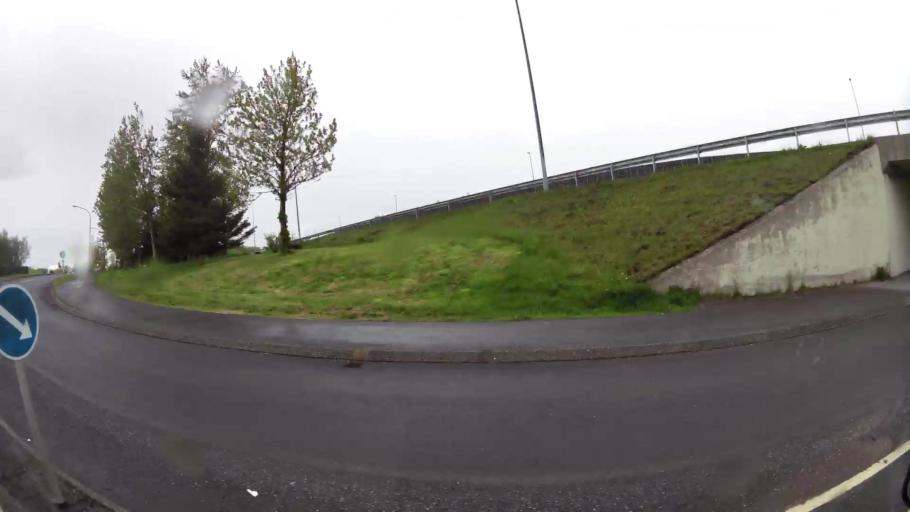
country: IS
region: Capital Region
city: Gardabaer
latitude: 64.0889
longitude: -21.8929
